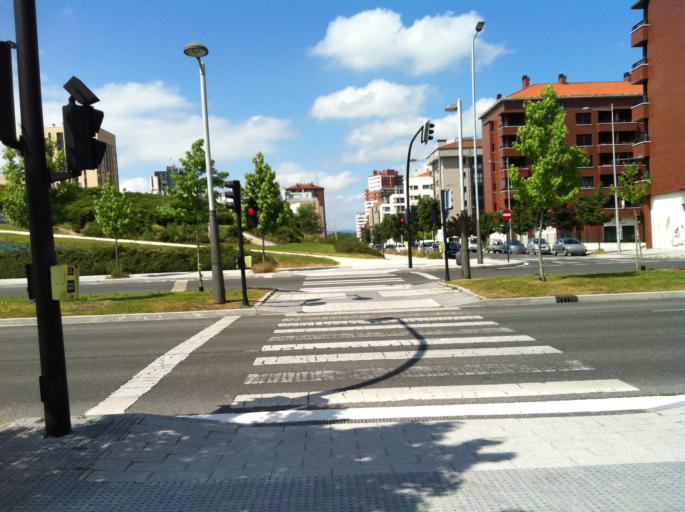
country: ES
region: Basque Country
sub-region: Provincia de Alava
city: Gasteiz / Vitoria
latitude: 42.8507
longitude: -2.6530
